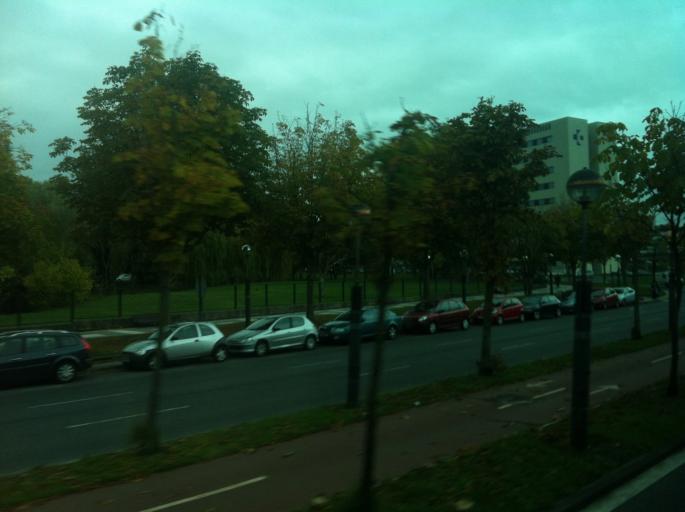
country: ES
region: Basque Country
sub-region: Provincia de Alava
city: Gasteiz / Vitoria
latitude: 42.8561
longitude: -2.6916
